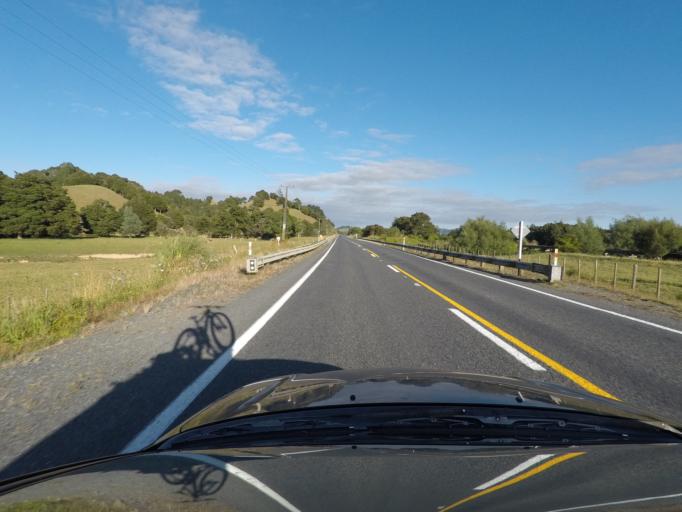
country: NZ
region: Northland
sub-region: Whangarei
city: Maungatapere
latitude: -35.5331
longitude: 174.2296
